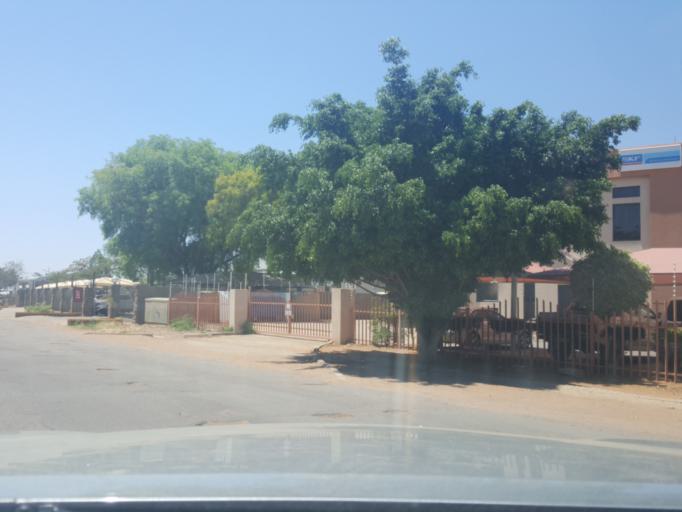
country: BW
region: South East
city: Gaborone
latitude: -24.6816
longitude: 25.8915
